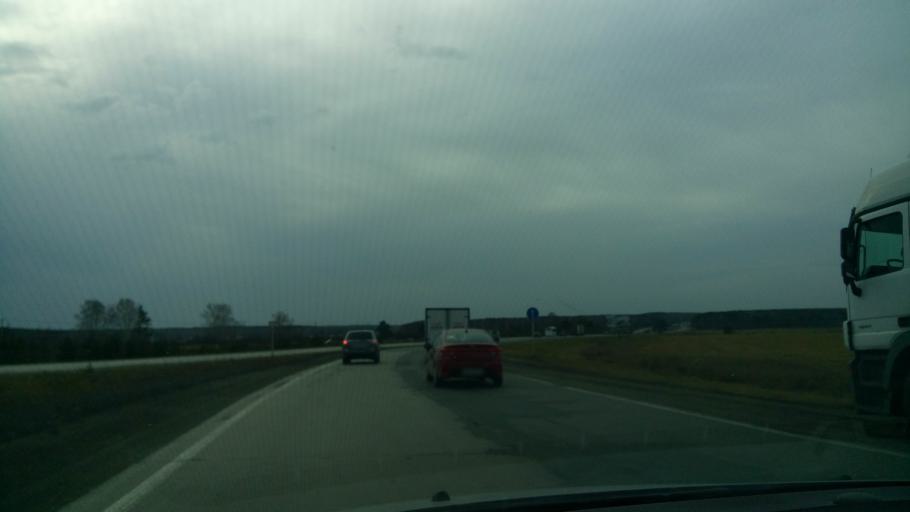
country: RU
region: Sverdlovsk
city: Verkhneye Dubrovo
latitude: 56.7372
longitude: 61.1013
